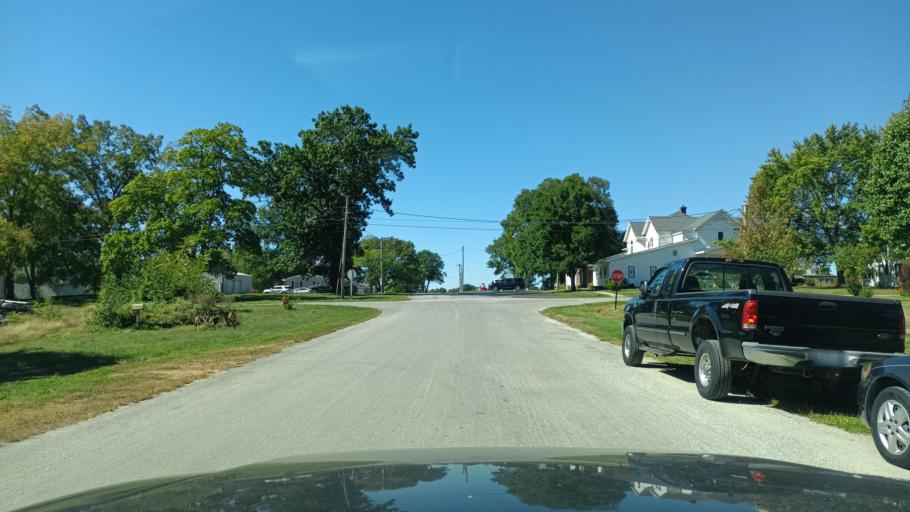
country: US
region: Missouri
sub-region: Macon County
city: La Plata
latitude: 40.0222
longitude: -92.4939
